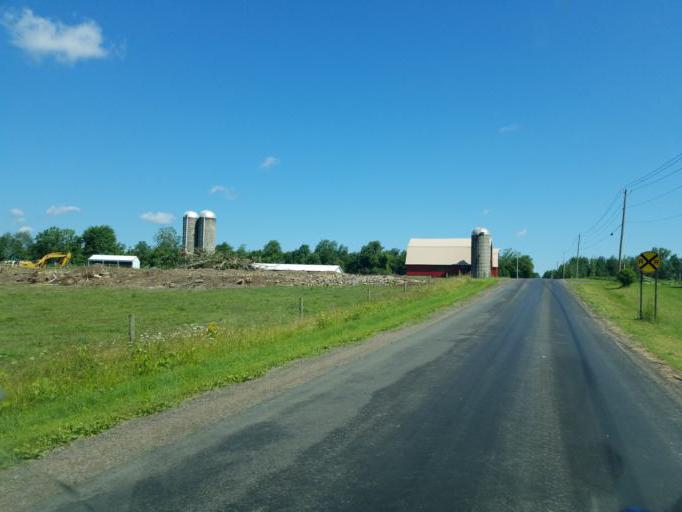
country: US
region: New York
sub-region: Wayne County
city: Wolcott
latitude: 43.1858
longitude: -76.8674
